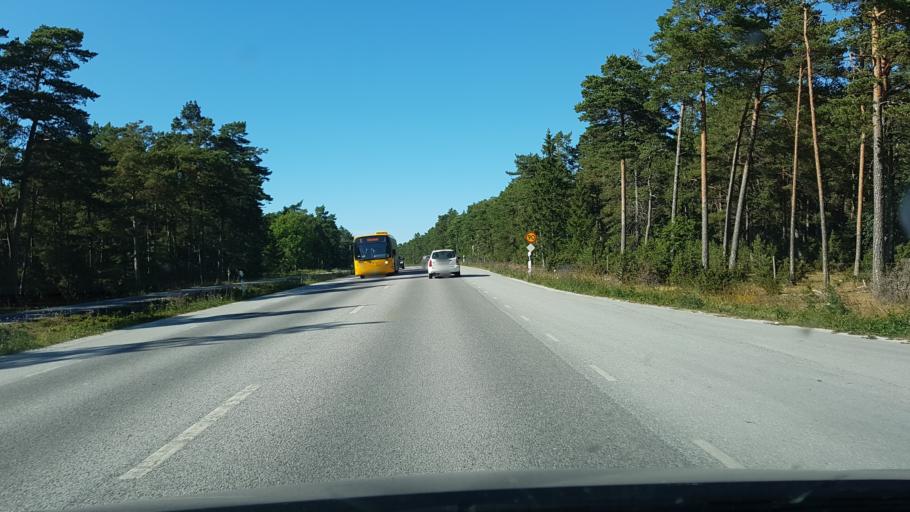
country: SE
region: Gotland
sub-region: Gotland
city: Vibble
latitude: 57.5531
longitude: 18.2030
